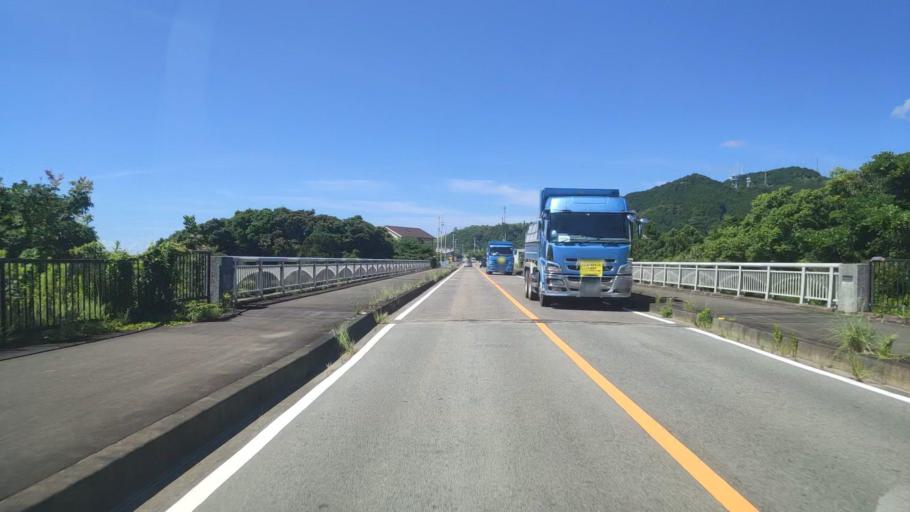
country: JP
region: Wakayama
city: Shingu
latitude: 33.7075
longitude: 135.9948
